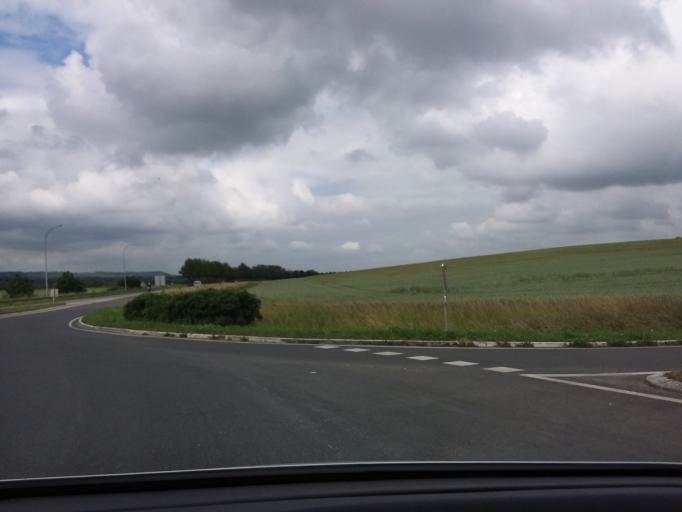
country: FR
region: Picardie
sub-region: Departement de l'Aisne
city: Bucy-le-Long
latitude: 49.3831
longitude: 3.4239
